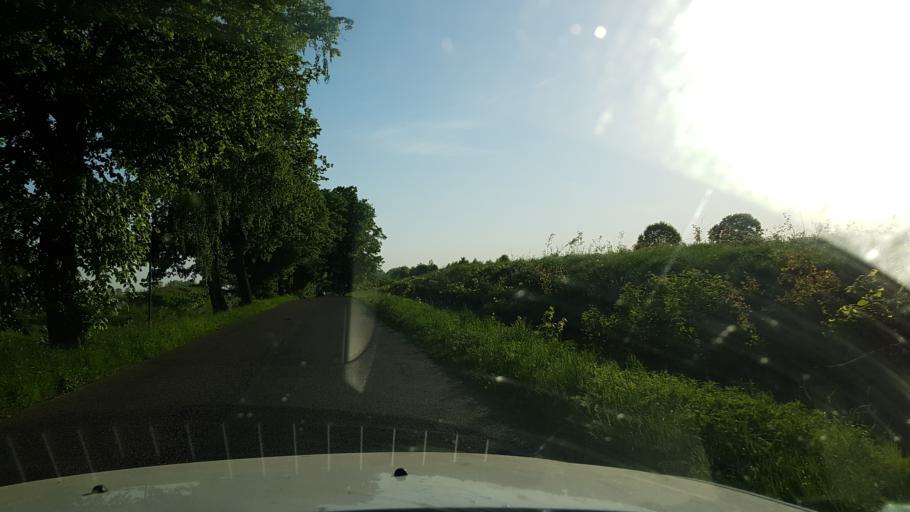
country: PL
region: West Pomeranian Voivodeship
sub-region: Powiat lobeski
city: Dobra
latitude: 53.5704
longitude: 15.2111
